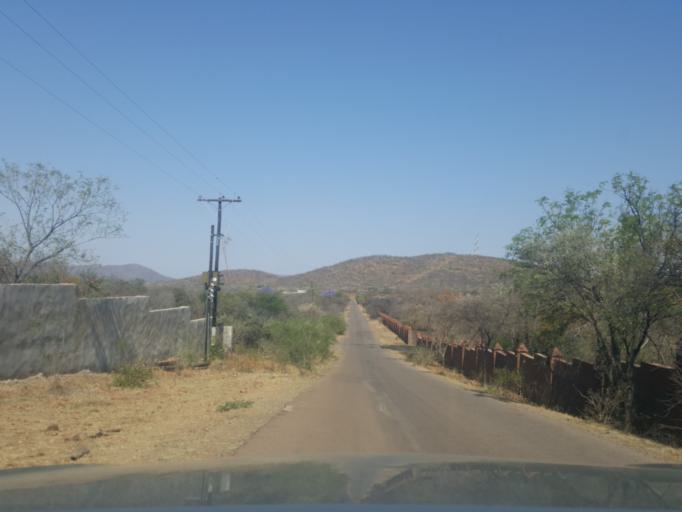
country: BW
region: Kweneng
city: Gabane
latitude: -24.7427
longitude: 25.8245
